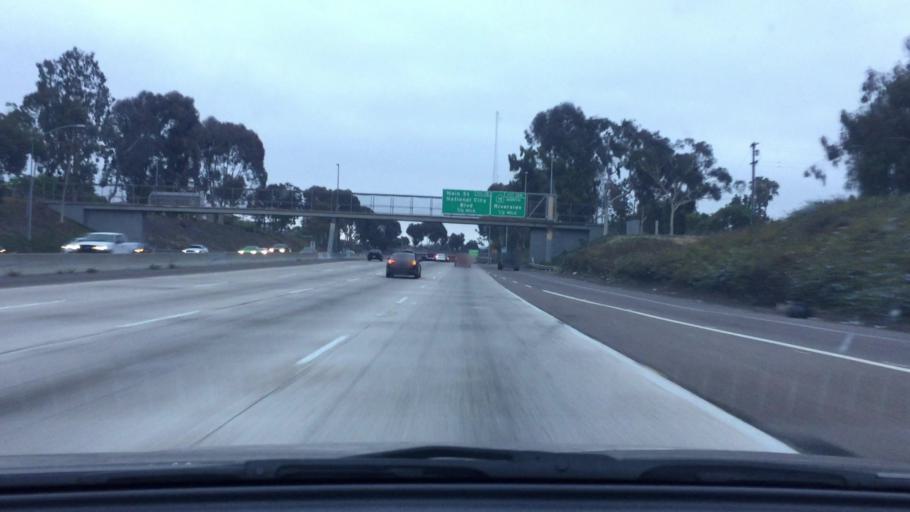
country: US
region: California
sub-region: San Diego County
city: San Diego
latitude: 32.6943
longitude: -117.1305
